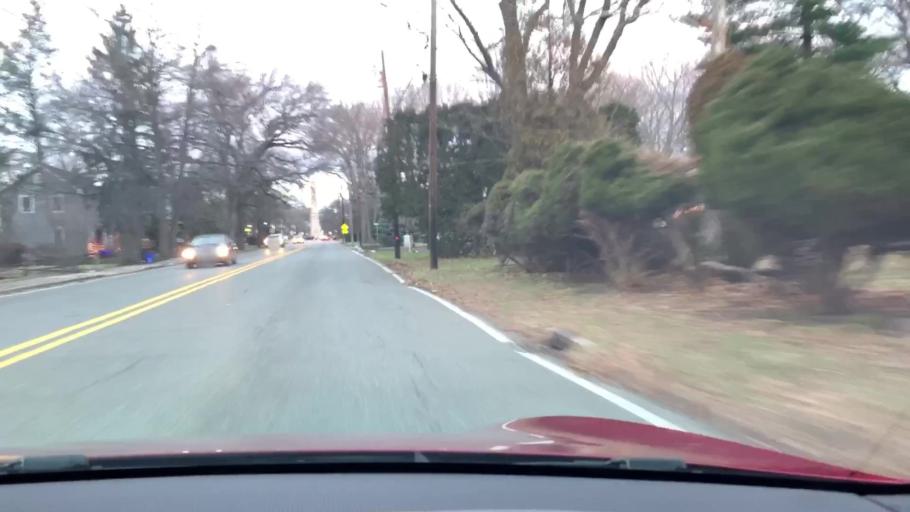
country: US
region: New Jersey
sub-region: Bergen County
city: Cresskill
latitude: 40.9387
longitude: -73.9771
